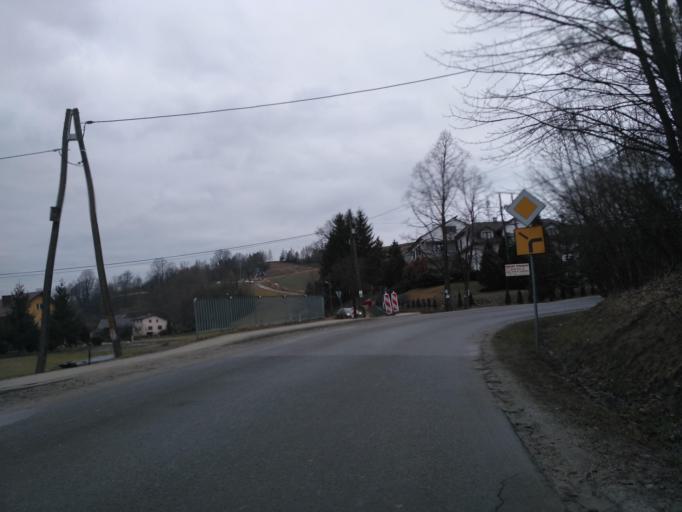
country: PL
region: Subcarpathian Voivodeship
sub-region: Powiat rzeszowski
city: Dynow
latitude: 49.8122
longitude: 22.2547
